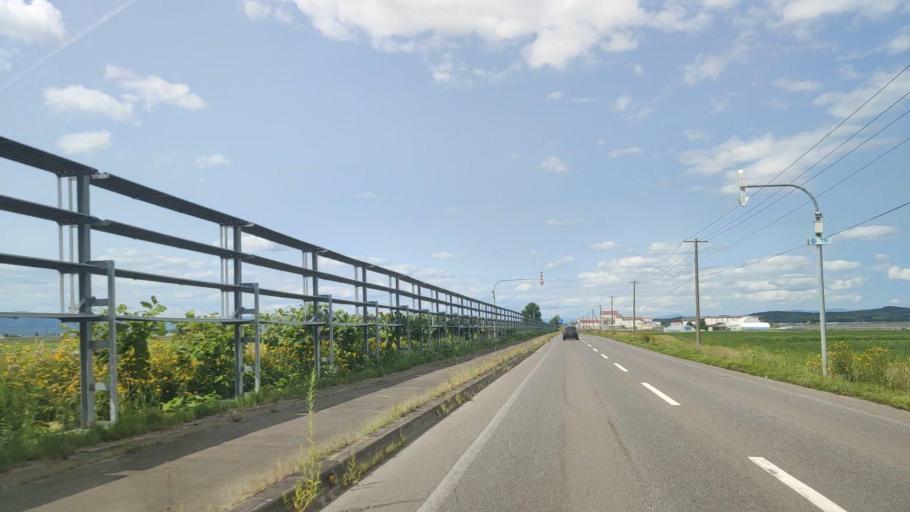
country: JP
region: Hokkaido
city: Nayoro
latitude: 44.1963
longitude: 142.4159
